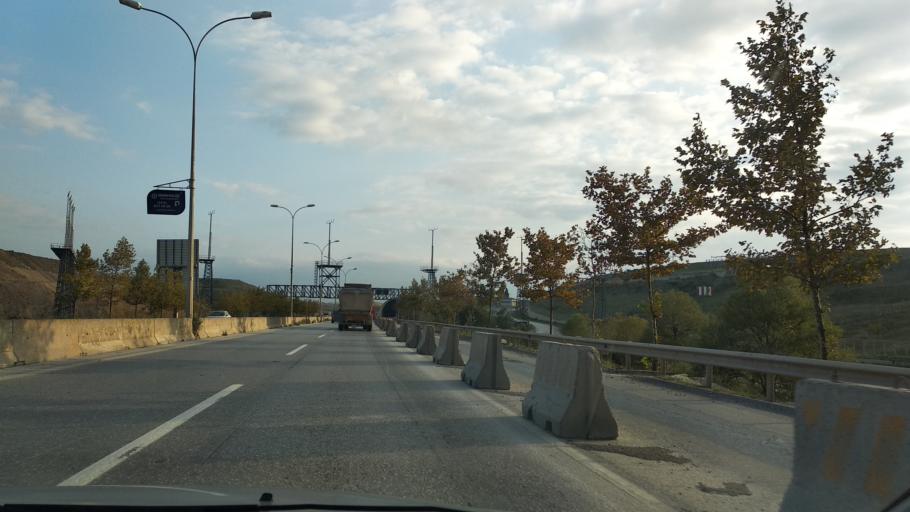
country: TR
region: Istanbul
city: Pendik
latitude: 40.9070
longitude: 29.3274
